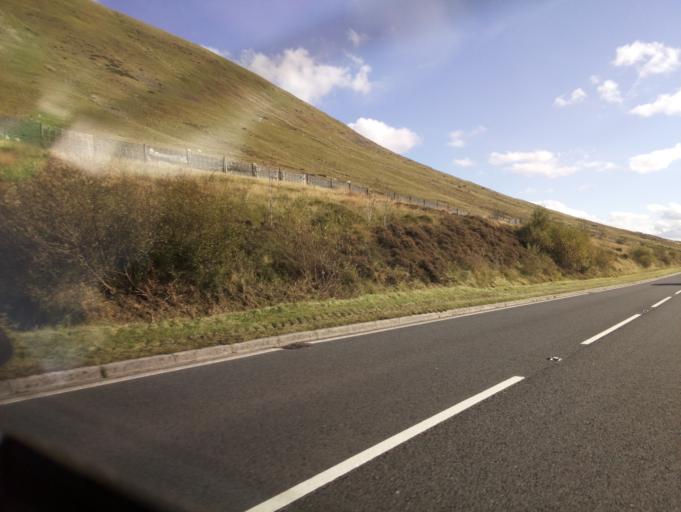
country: GB
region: Wales
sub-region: Sir Powys
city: Brecon
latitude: 51.8580
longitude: -3.4702
